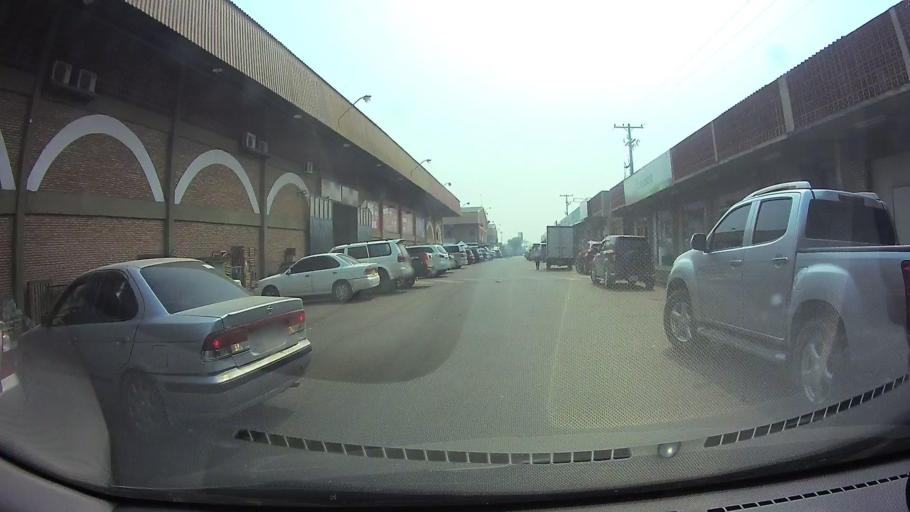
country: PY
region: Central
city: Limpio
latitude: -25.1785
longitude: -57.4826
